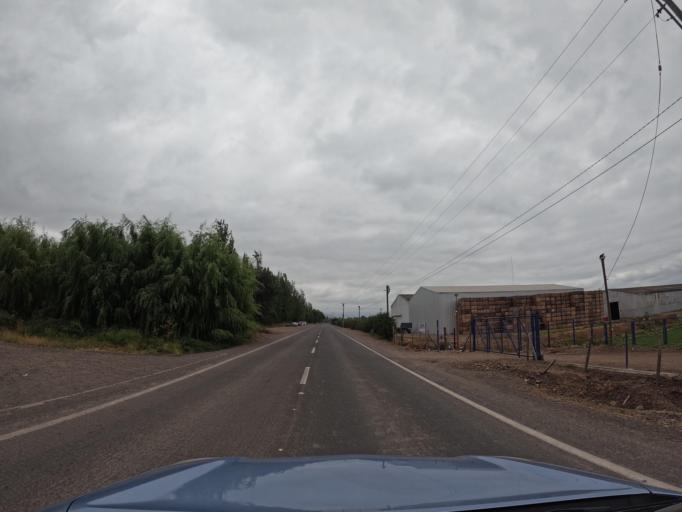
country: CL
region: O'Higgins
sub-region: Provincia de Colchagua
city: Chimbarongo
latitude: -34.7265
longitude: -71.0810
